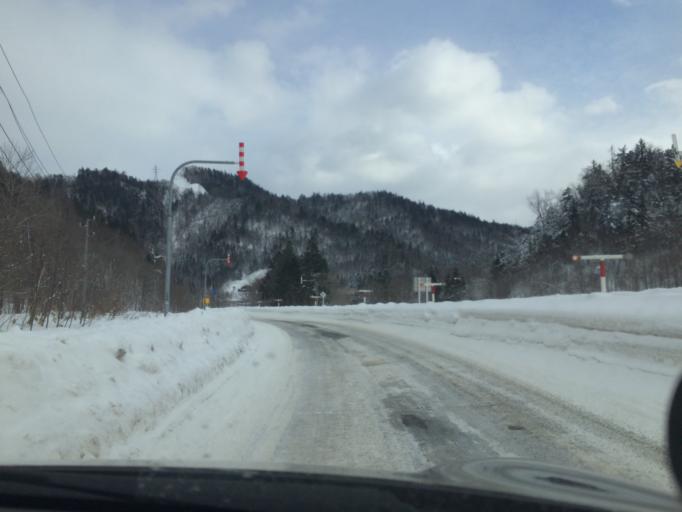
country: JP
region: Hokkaido
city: Shimo-furano
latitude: 43.0471
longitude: 142.4766
